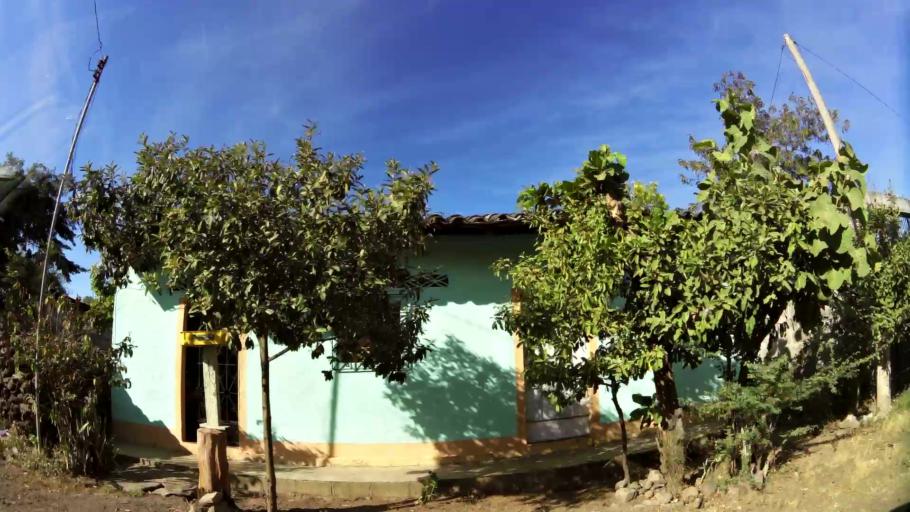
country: SV
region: San Miguel
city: San Miguel
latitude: 13.4660
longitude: -88.1924
